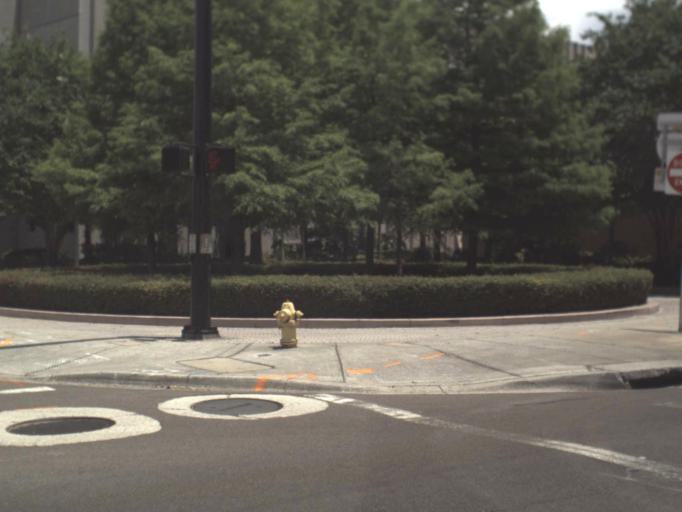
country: US
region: Florida
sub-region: Duval County
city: Jacksonville
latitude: 30.3273
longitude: -81.6654
